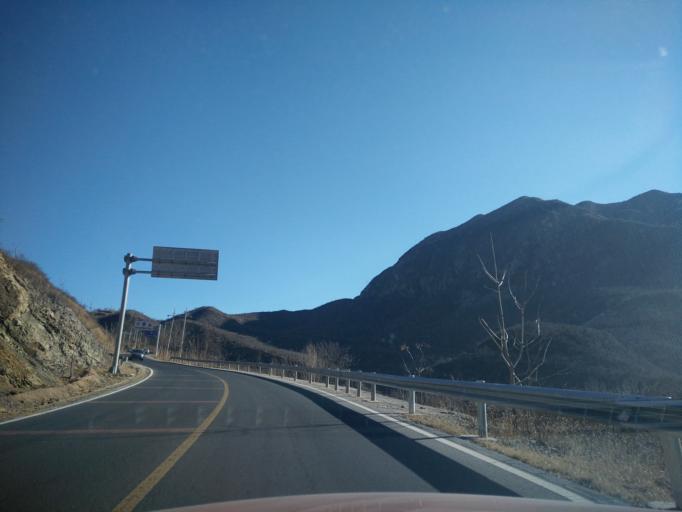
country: CN
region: Beijing
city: Zhaitang
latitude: 40.0066
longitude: 115.6987
